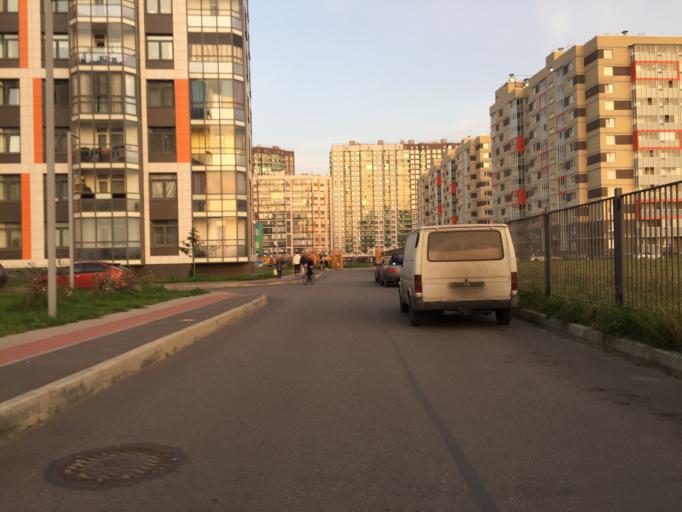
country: RU
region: St.-Petersburg
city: Grazhdanka
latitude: 60.0577
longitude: 30.4159
